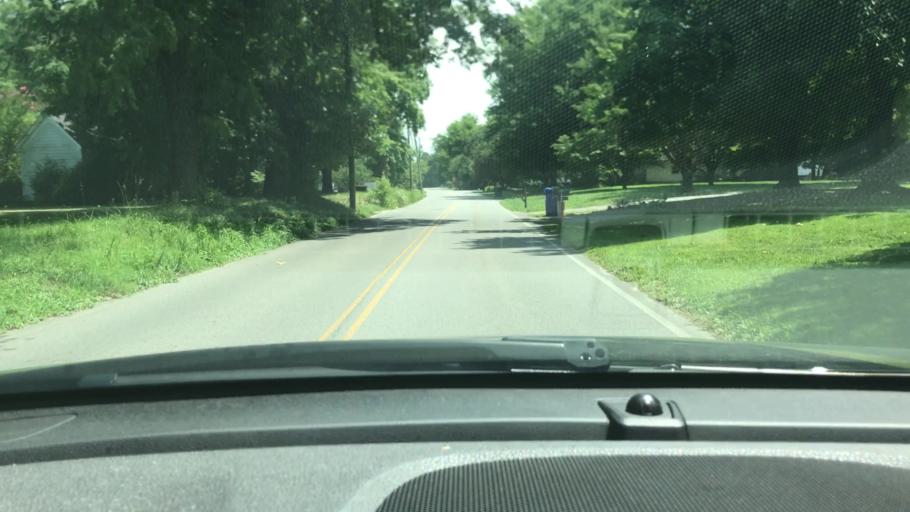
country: US
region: Tennessee
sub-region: Sumner County
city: White House
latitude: 36.4691
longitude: -86.6496
